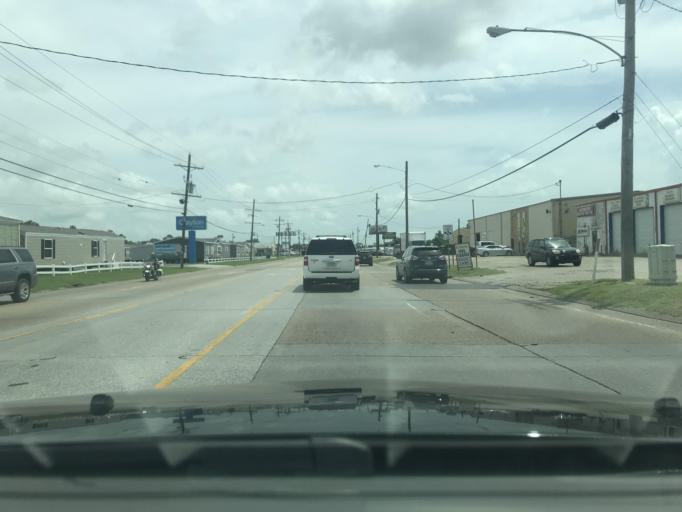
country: US
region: Louisiana
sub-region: Calcasieu Parish
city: Lake Charles
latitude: 30.2270
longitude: -93.1802
